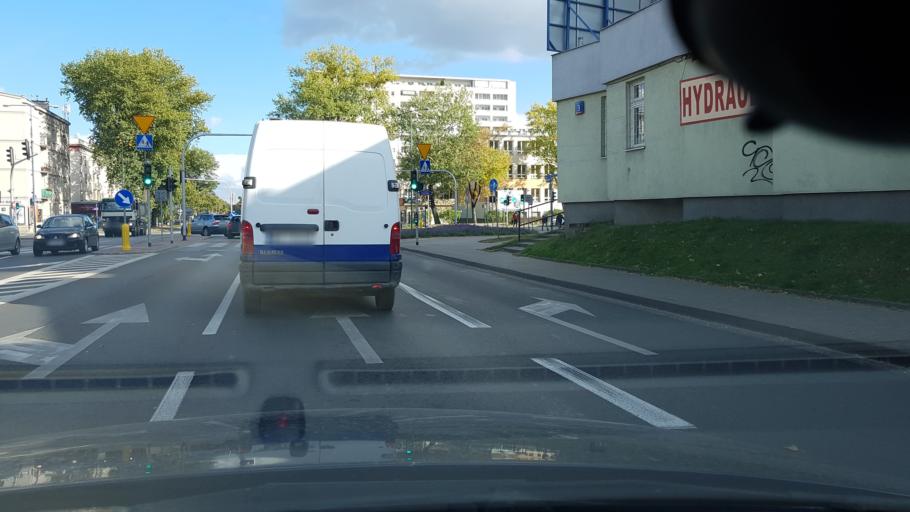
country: PL
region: Masovian Voivodeship
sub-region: Warszawa
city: Bielany
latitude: 52.2781
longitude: 20.9382
